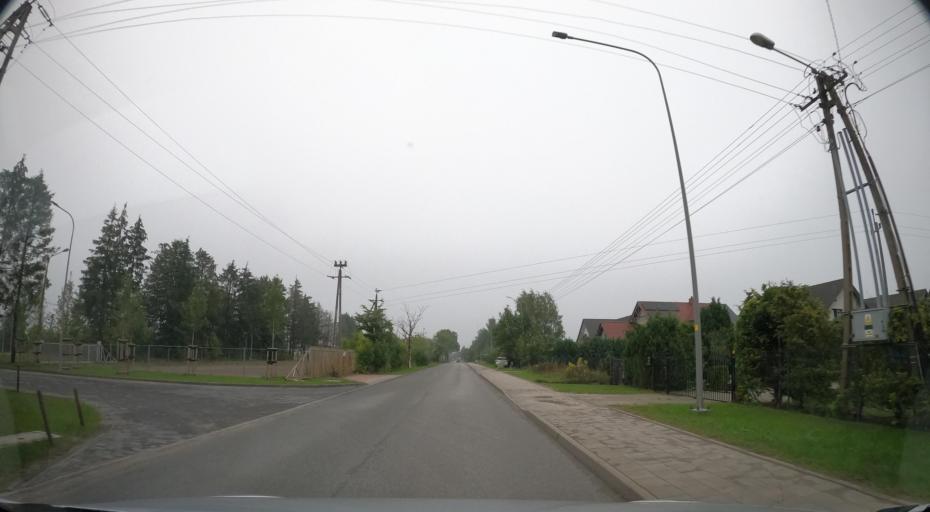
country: PL
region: Pomeranian Voivodeship
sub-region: Powiat kartuski
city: Chwaszczyno
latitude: 54.4217
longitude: 18.4538
